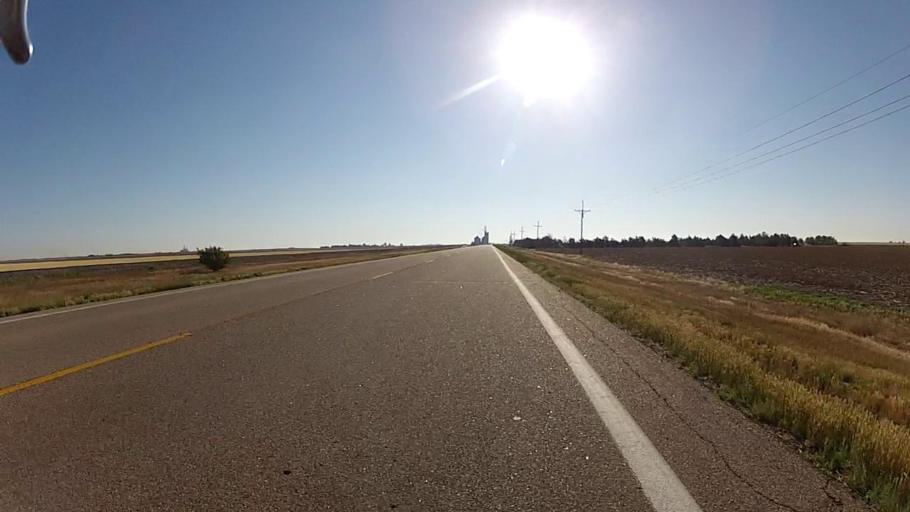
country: US
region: Kansas
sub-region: Haskell County
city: Sublette
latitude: 37.5125
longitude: -100.7388
